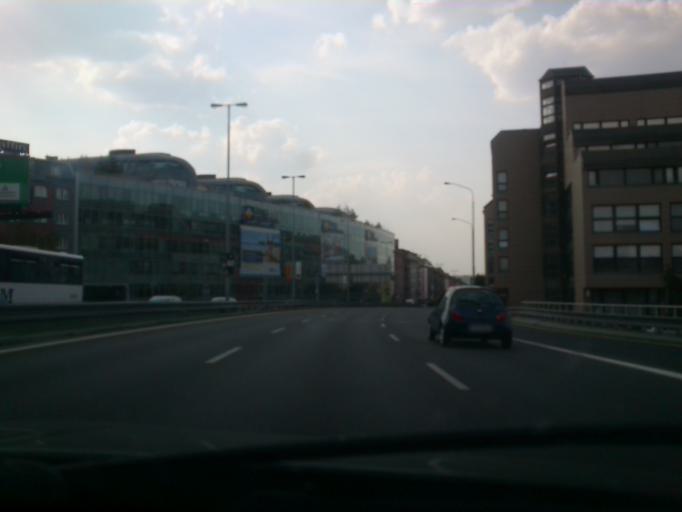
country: CZ
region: Praha
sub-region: Praha 2
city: Vysehrad
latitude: 50.0529
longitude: 14.4415
